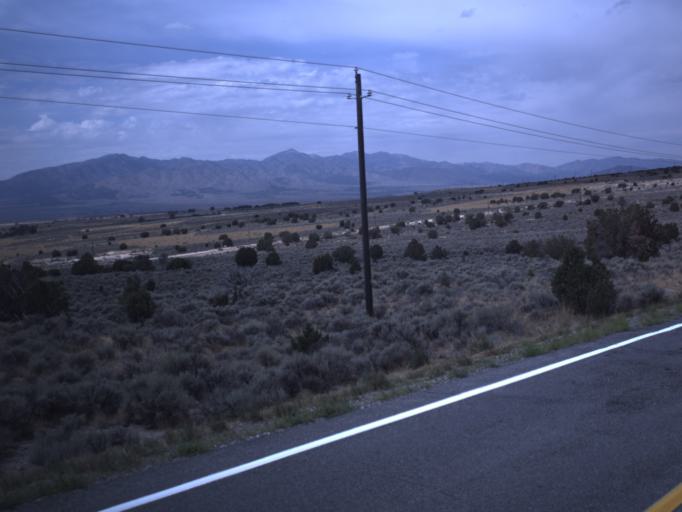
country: US
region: Utah
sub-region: Tooele County
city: Tooele
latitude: 40.3188
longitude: -112.2854
